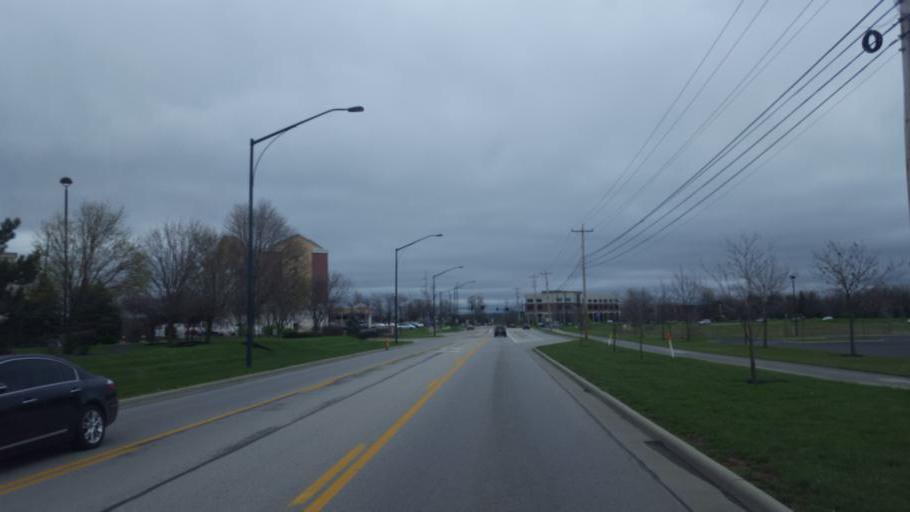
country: US
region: Ohio
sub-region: Franklin County
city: Westerville
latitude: 40.1372
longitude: -82.9677
